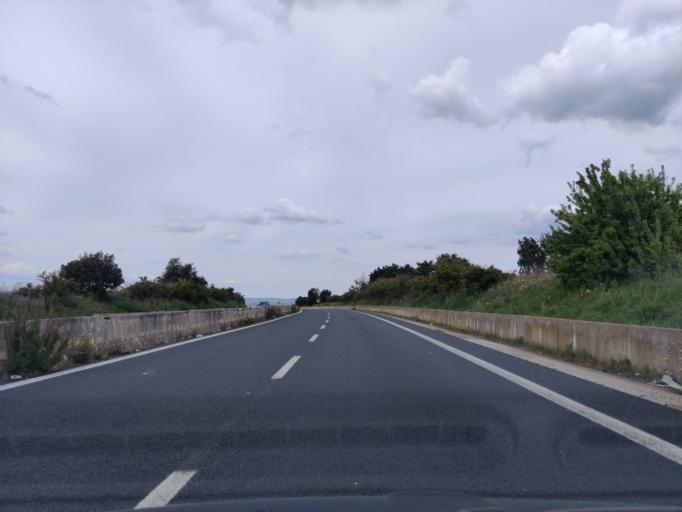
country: IT
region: Latium
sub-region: Citta metropolitana di Roma Capitale
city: Aurelia
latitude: 42.1350
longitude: 11.7948
